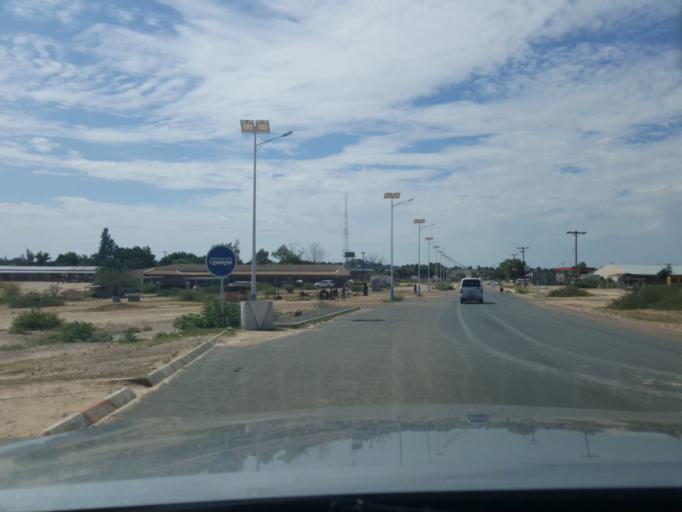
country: BW
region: Kweneng
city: Letlhakeng
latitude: -24.0993
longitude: 25.0295
